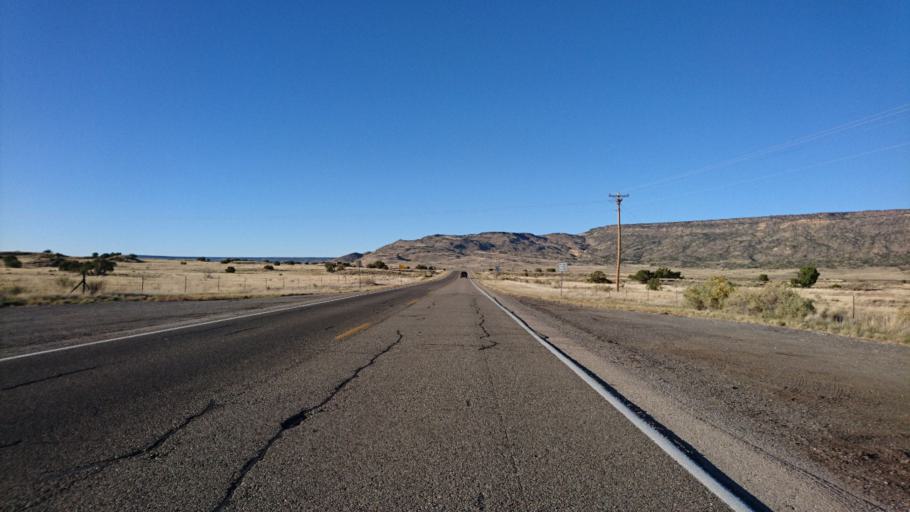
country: US
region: New Mexico
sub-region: Cibola County
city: Grants
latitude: 35.0886
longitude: -107.7700
